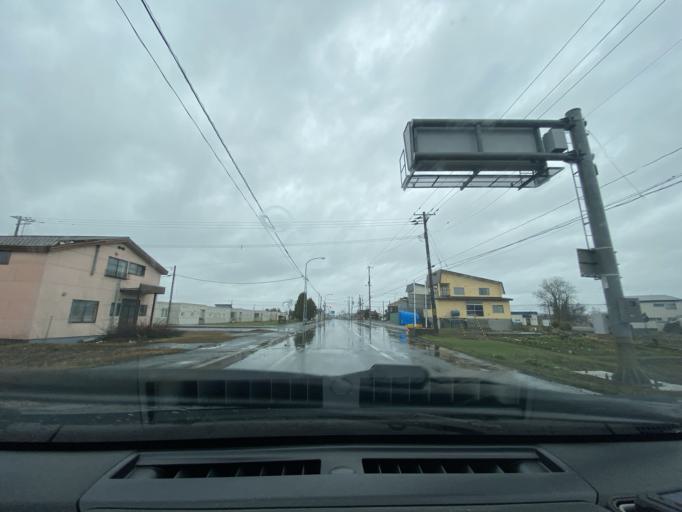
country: JP
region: Hokkaido
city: Fukagawa
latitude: 43.8086
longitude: 142.0295
